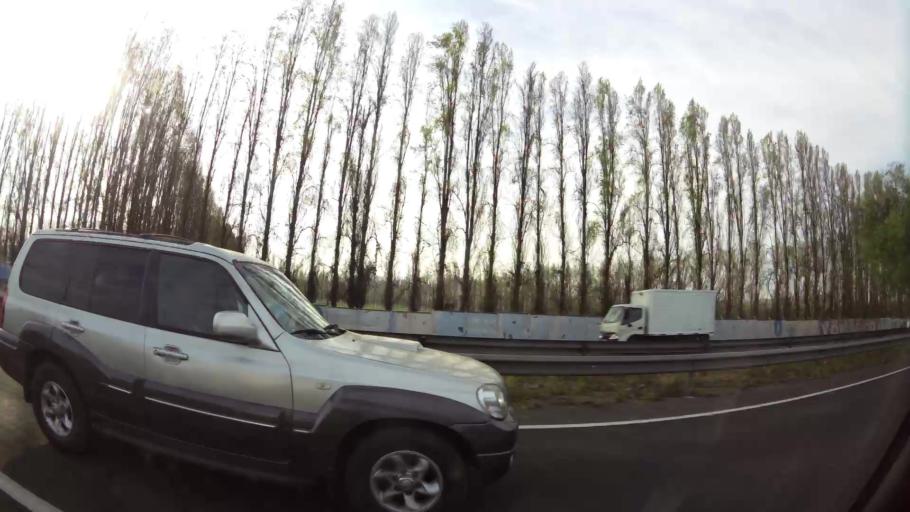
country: CL
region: Santiago Metropolitan
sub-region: Provincia de Talagante
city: Penaflor
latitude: -33.6311
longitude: -70.8669
